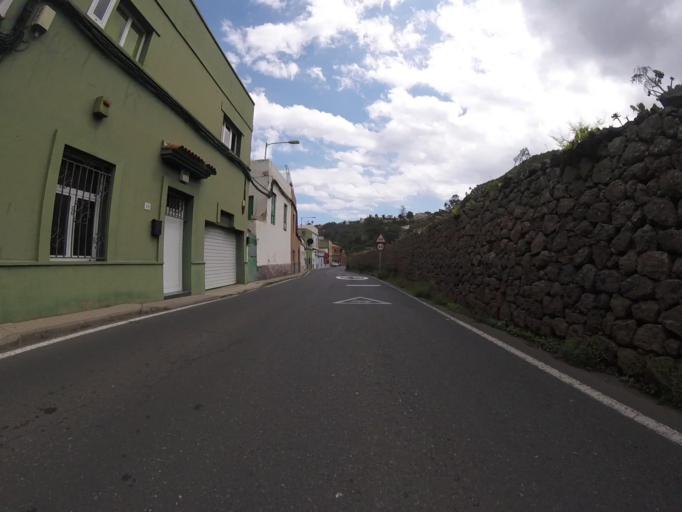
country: ES
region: Canary Islands
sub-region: Provincia de Las Palmas
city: Santa Brigida
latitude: 28.0588
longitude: -15.4685
